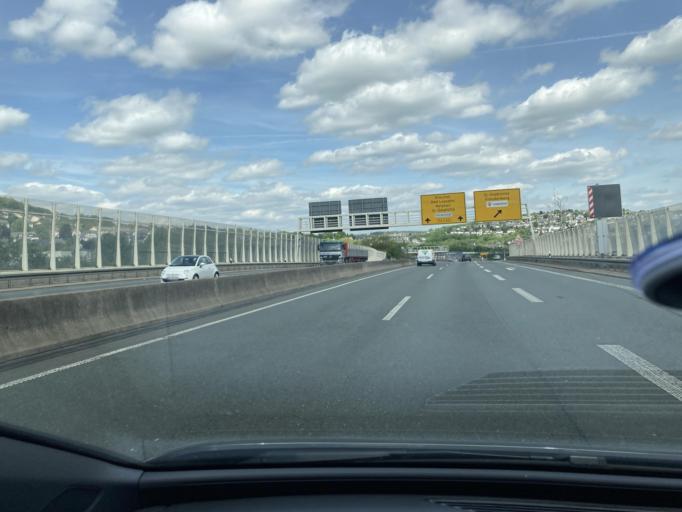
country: DE
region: North Rhine-Westphalia
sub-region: Regierungsbezirk Arnsberg
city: Siegen
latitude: 50.8759
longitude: 8.0141
